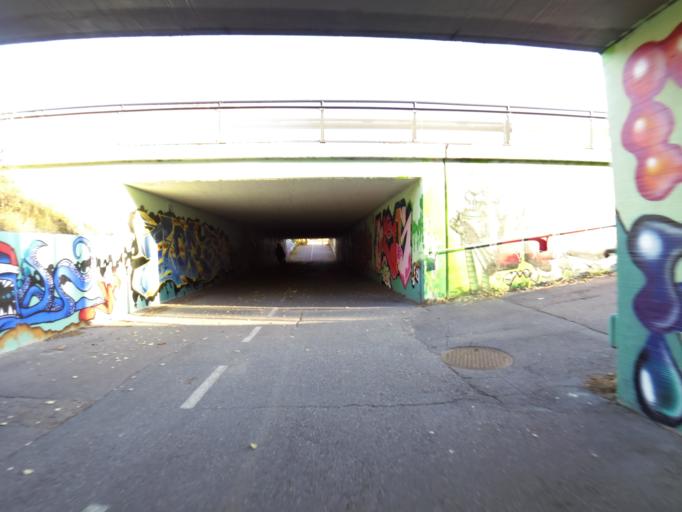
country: FI
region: Uusimaa
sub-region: Helsinki
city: Vantaa
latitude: 60.1995
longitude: 25.0369
